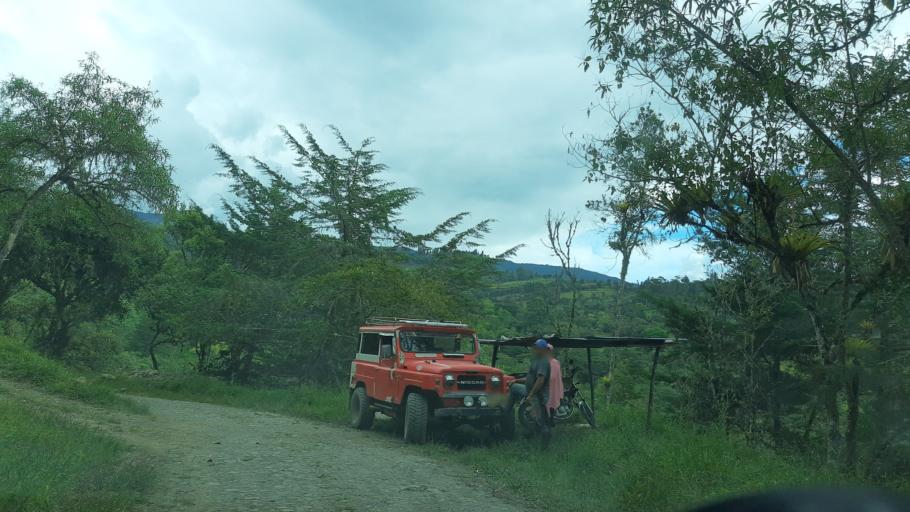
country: CO
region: Boyaca
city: Garagoa
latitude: 5.0406
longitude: -73.3342
